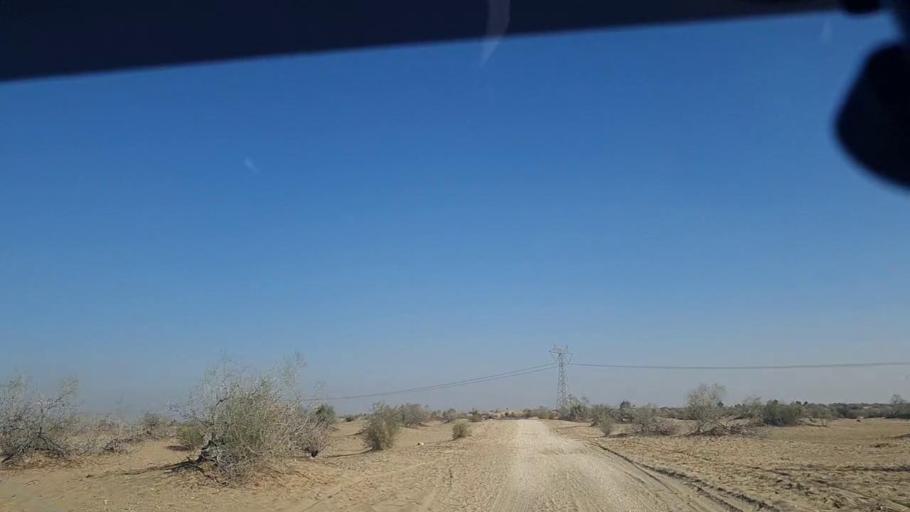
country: PK
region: Sindh
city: Khanpur
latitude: 27.6458
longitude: 69.4001
